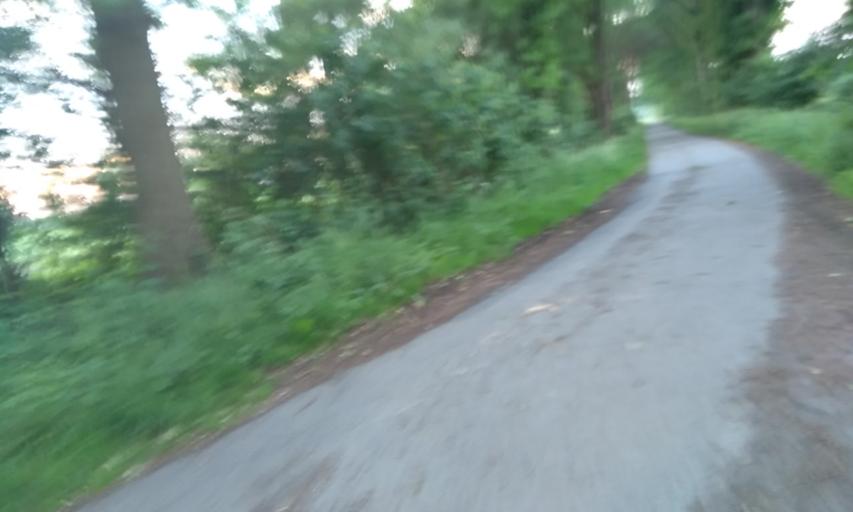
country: DE
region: Lower Saxony
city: Agathenburg
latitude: 53.5302
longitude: 9.4937
